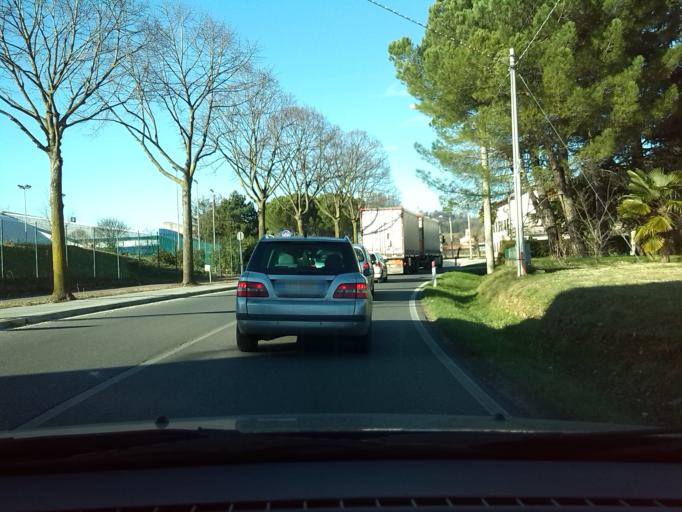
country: IT
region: Friuli Venezia Giulia
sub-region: Provincia di Gorizia
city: Cormons
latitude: 45.9670
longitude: 13.4592
